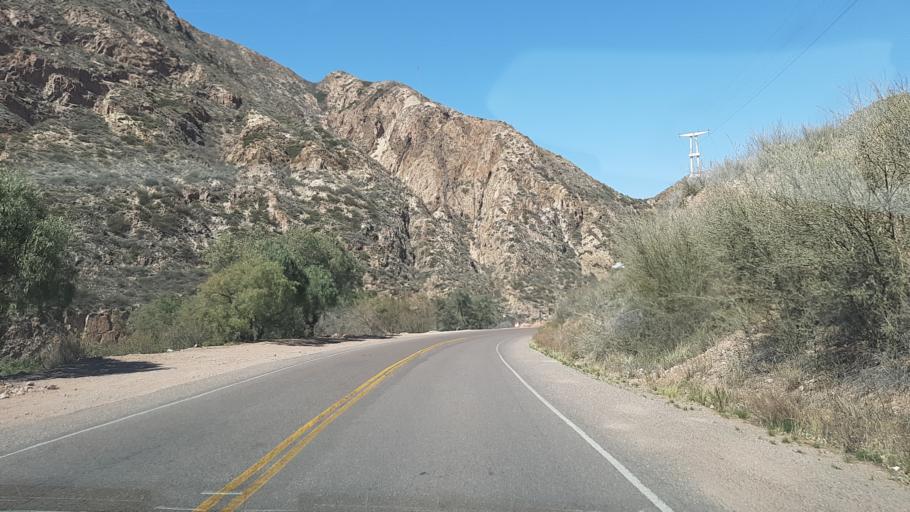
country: AR
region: Mendoza
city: Lujan de Cuyo
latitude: -33.0205
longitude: -69.1153
